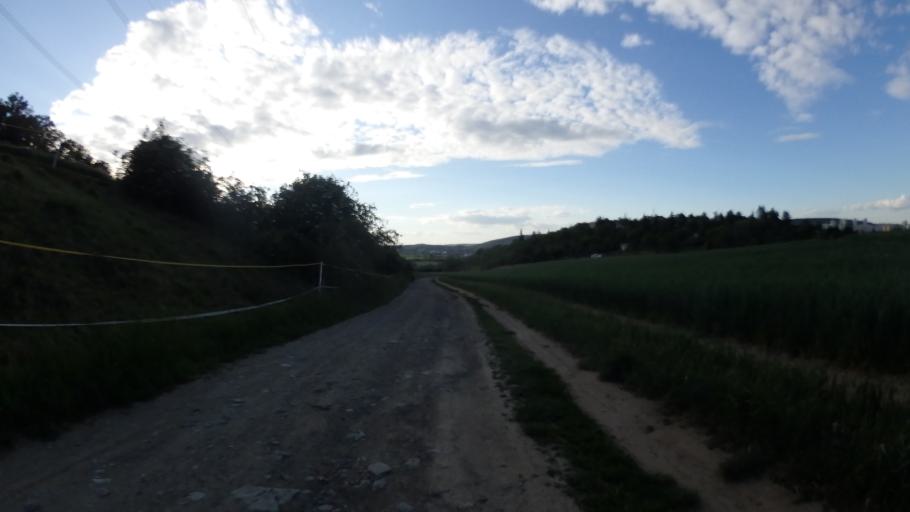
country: CZ
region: South Moravian
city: Ostopovice
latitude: 49.1566
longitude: 16.5420
